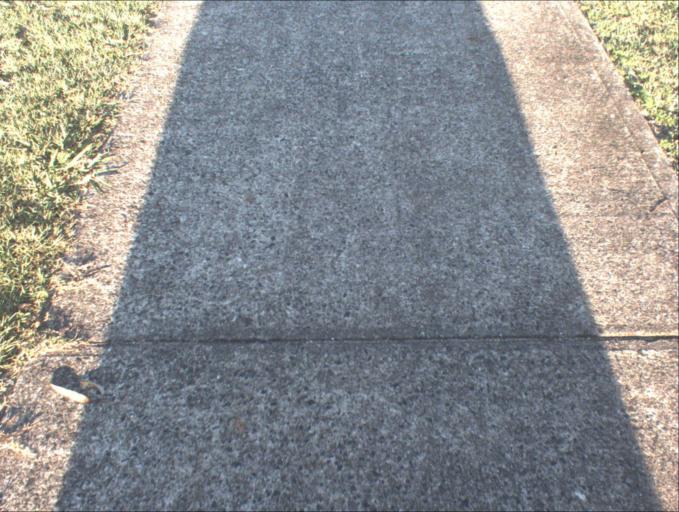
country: AU
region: Queensland
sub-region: Logan
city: Chambers Flat
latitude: -27.7668
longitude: 153.1162
